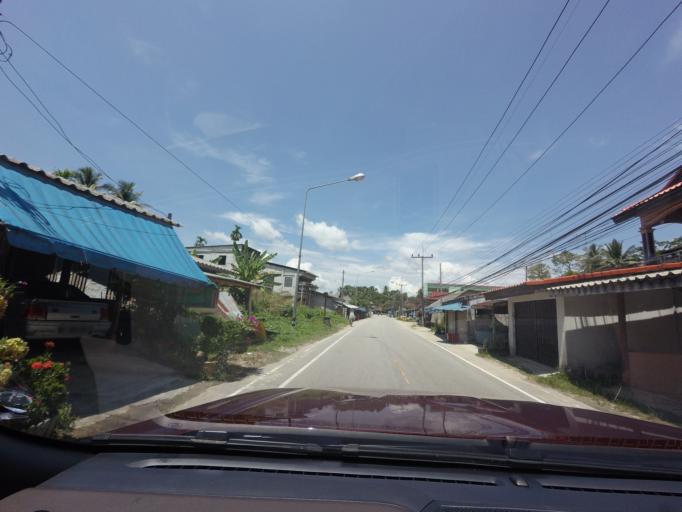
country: TH
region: Narathiwat
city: Chanae
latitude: 6.1274
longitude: 101.6986
